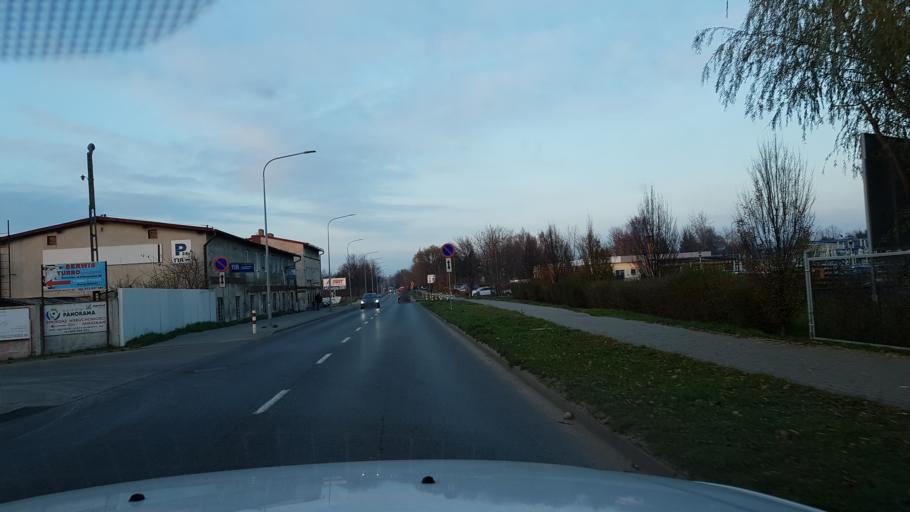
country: PL
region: West Pomeranian Voivodeship
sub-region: Koszalin
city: Koszalin
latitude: 54.1772
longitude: 16.1848
